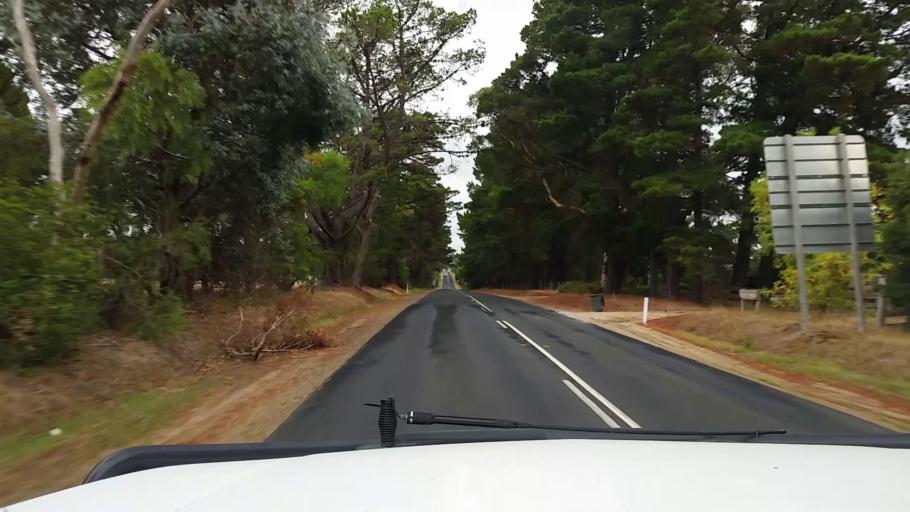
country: AU
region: Victoria
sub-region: Mornington Peninsula
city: Balnarring
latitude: -38.3519
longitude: 145.1457
